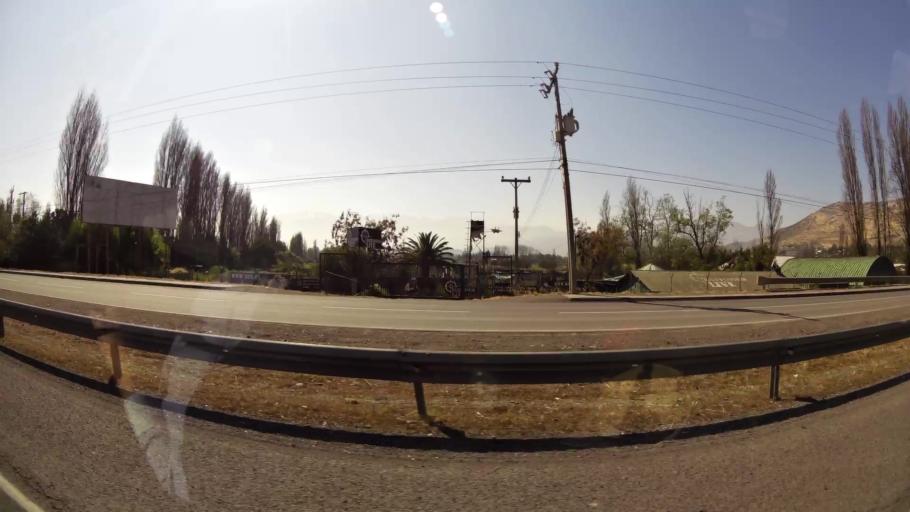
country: CL
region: Santiago Metropolitan
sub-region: Provincia de Chacabuco
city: Chicureo Abajo
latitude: -33.3003
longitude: -70.7001
